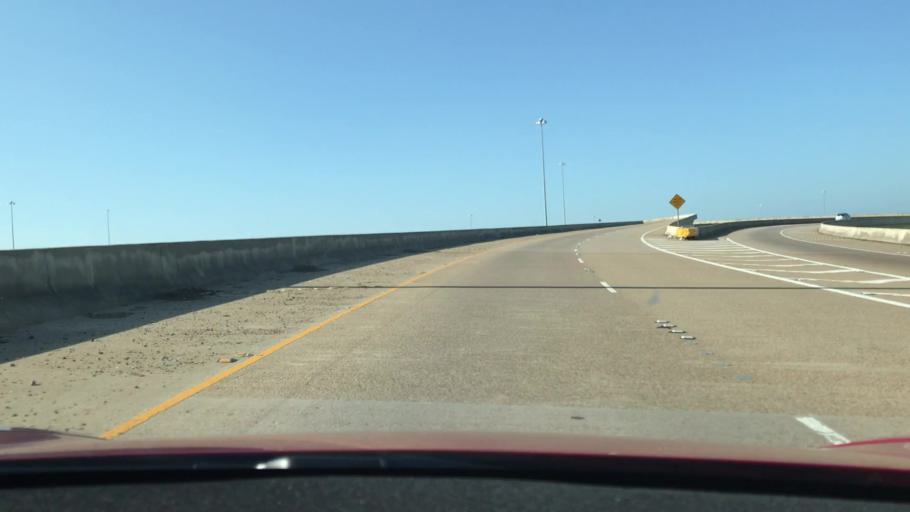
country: US
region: Louisiana
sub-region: Bossier Parish
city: Bossier City
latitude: 32.4227
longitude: -93.7499
